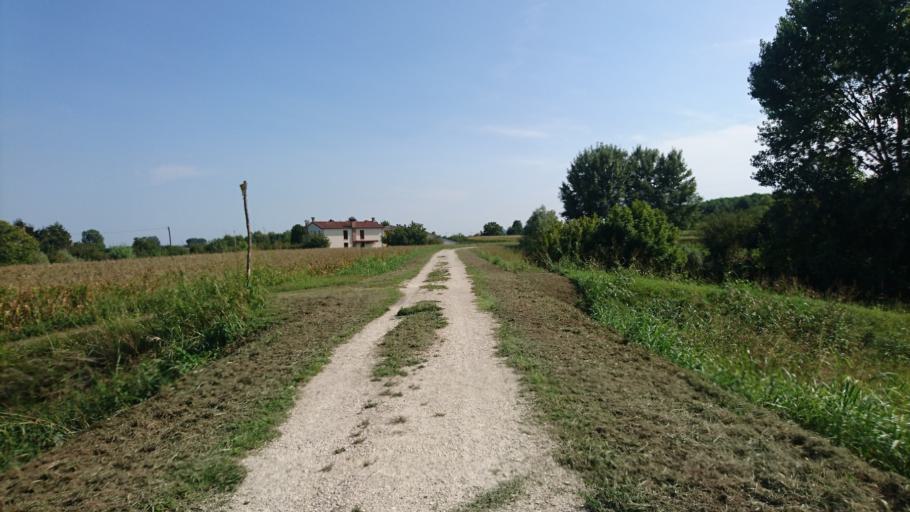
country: IT
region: Veneto
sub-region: Provincia di Padova
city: Veggiano
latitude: 45.4441
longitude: 11.7263
